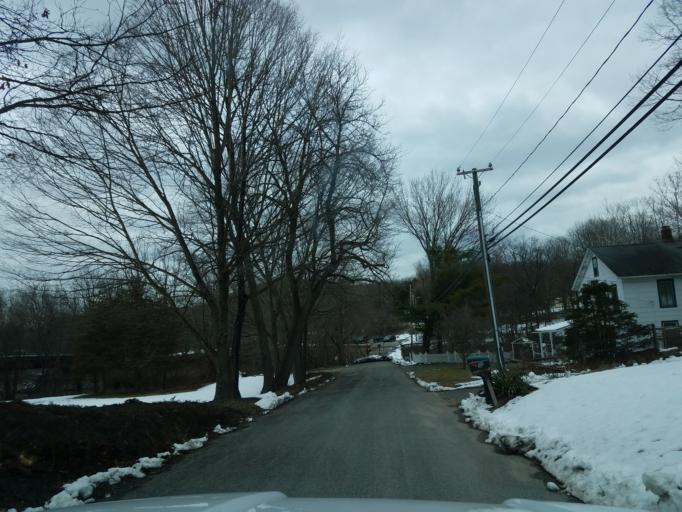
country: US
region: Connecticut
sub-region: Litchfield County
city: New Milford
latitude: 41.5403
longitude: -73.4135
